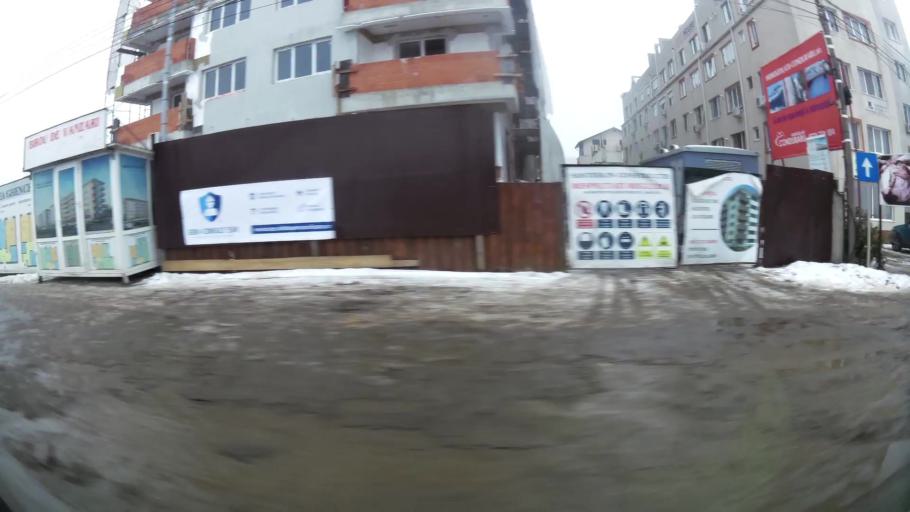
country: RO
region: Ilfov
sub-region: Comuna Bragadiru
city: Bragadiru
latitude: 44.4082
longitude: 25.9918
